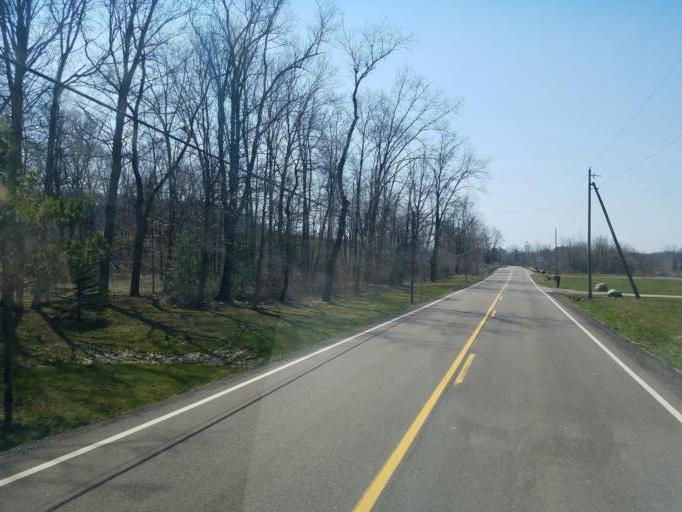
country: US
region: Ohio
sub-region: Knox County
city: Danville
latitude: 40.5071
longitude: -82.2867
